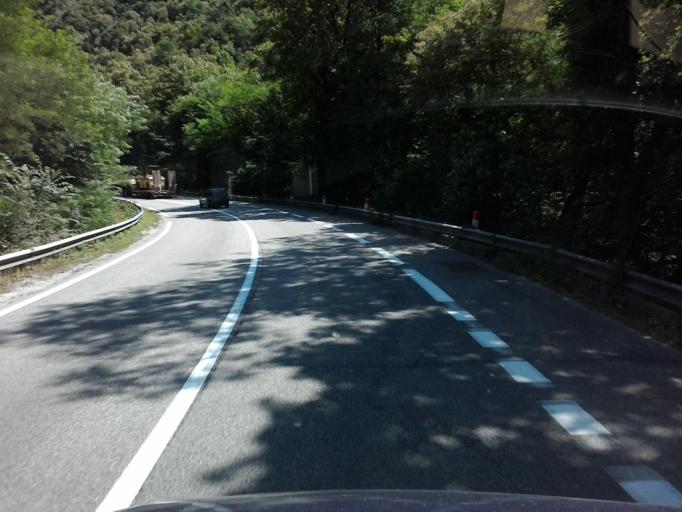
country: FR
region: Rhone-Alpes
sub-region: Departement de l'Isere
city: Vaulnaveys-le-Bas
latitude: 45.0537
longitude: 5.8507
